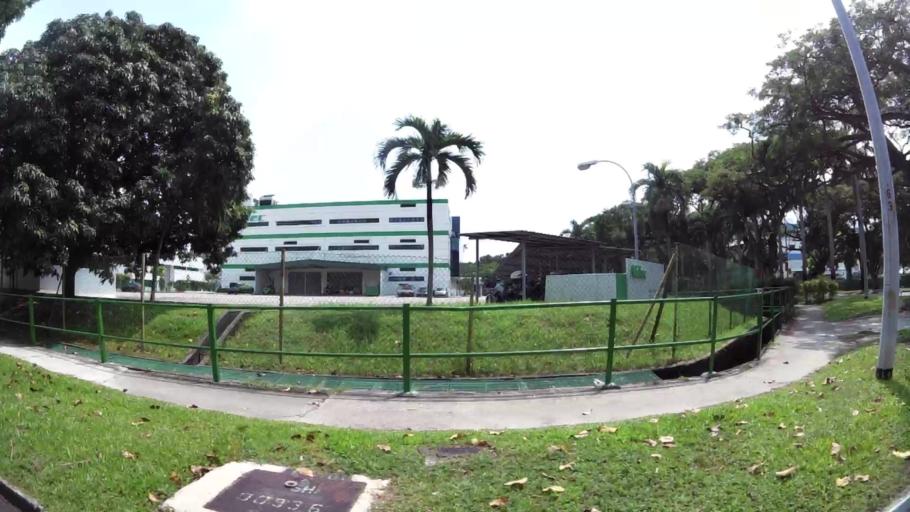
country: MY
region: Johor
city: Kampung Pasir Gudang Baru
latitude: 1.3754
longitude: 103.9738
